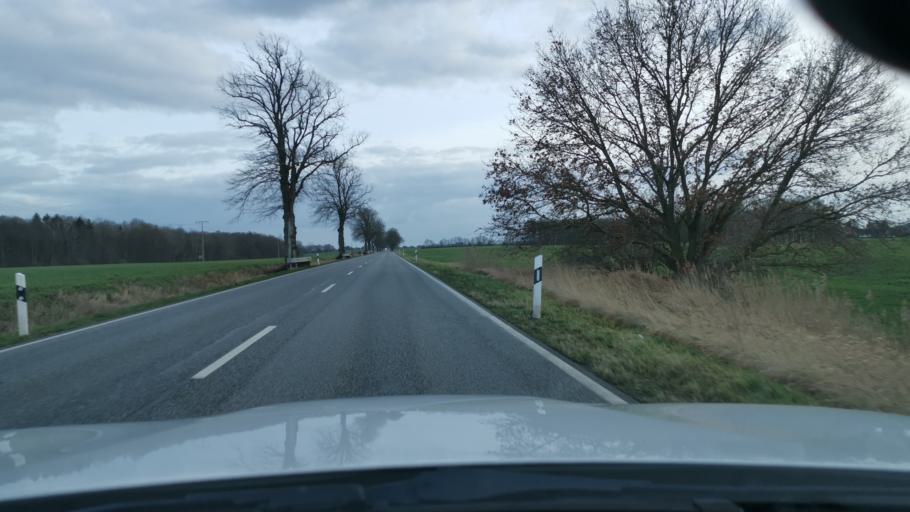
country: DE
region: Mecklenburg-Vorpommern
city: Dummerstorf
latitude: 53.9919
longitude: 12.2687
